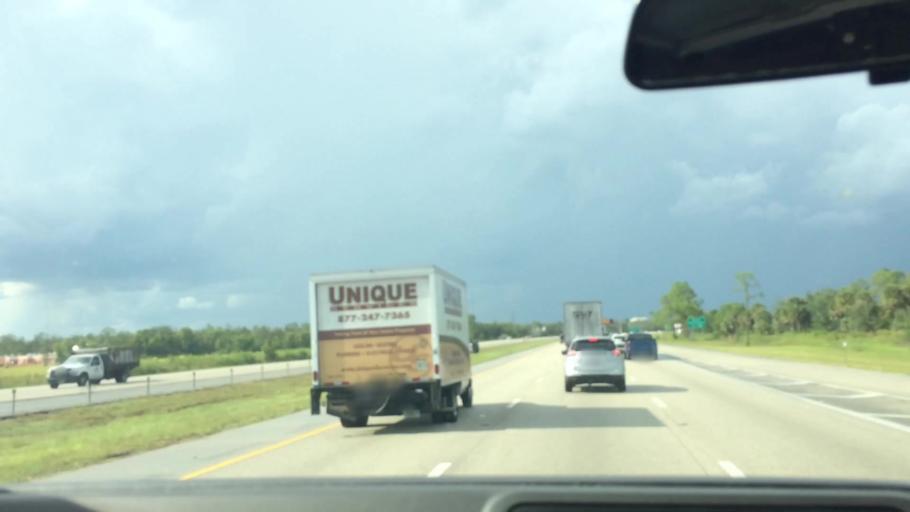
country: US
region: Florida
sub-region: Lee County
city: Fort Myers
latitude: 26.6167
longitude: -81.8039
